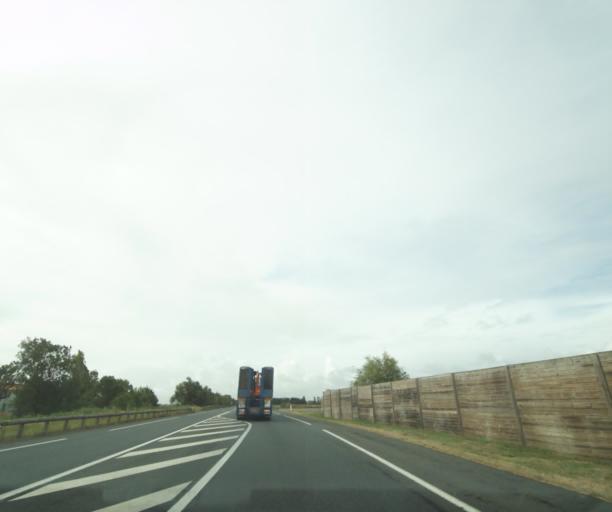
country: FR
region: Pays de la Loire
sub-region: Departement de la Vendee
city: Champagne-les-Marais
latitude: 46.4095
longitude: -1.0986
